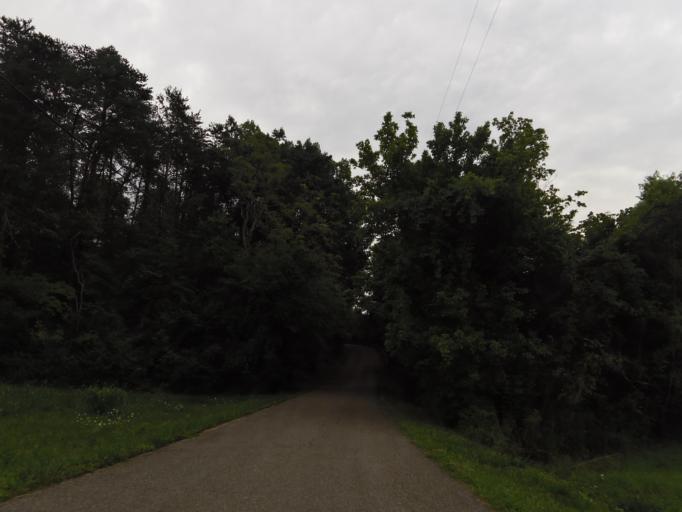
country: US
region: Tennessee
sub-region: Sevier County
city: Seymour
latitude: 35.9434
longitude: -83.7970
